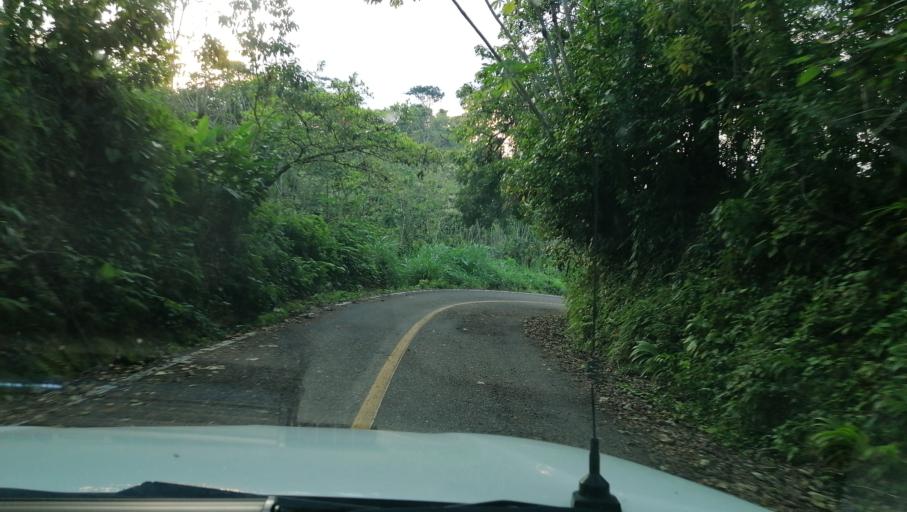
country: MX
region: Chiapas
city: Pichucalco
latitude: 17.5101
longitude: -93.2111
